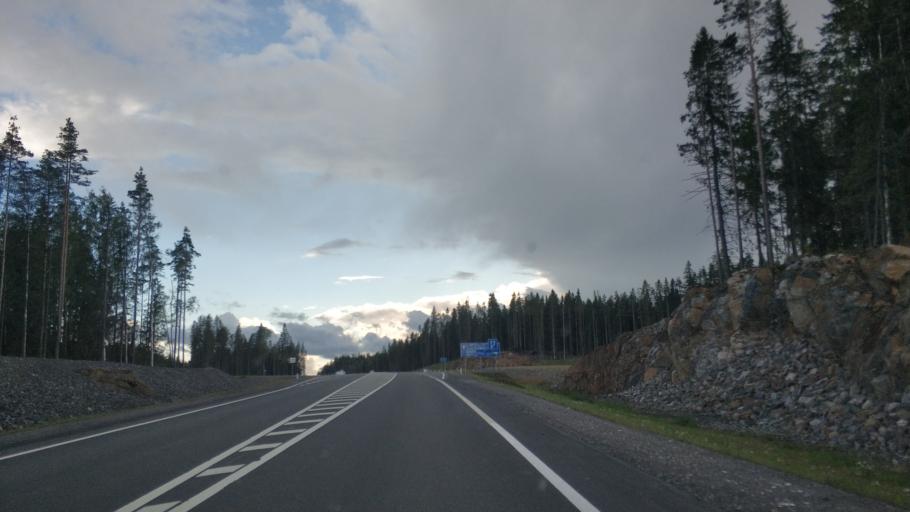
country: RU
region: Republic of Karelia
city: Lakhdenpokh'ya
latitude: 61.4673
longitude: 30.0018
